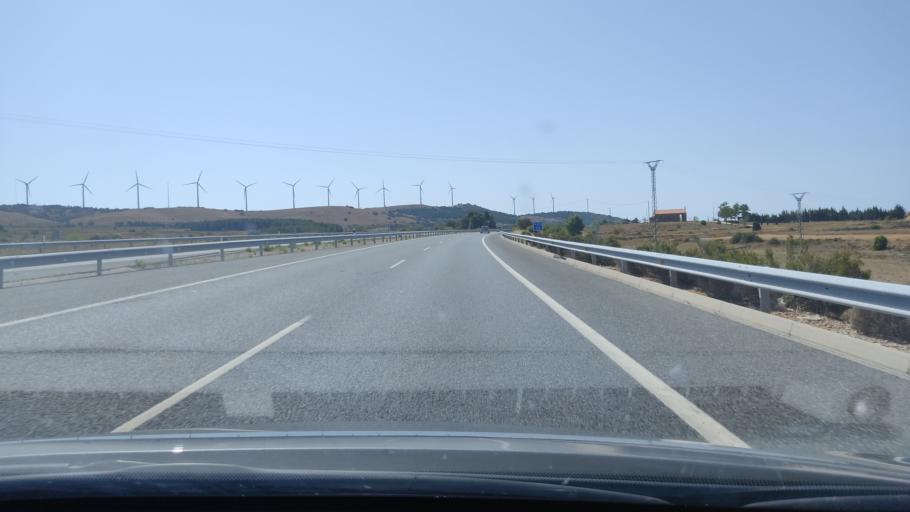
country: ES
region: Valencia
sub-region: Provincia de Castello
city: Barracas
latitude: 40.0173
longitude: -0.6922
